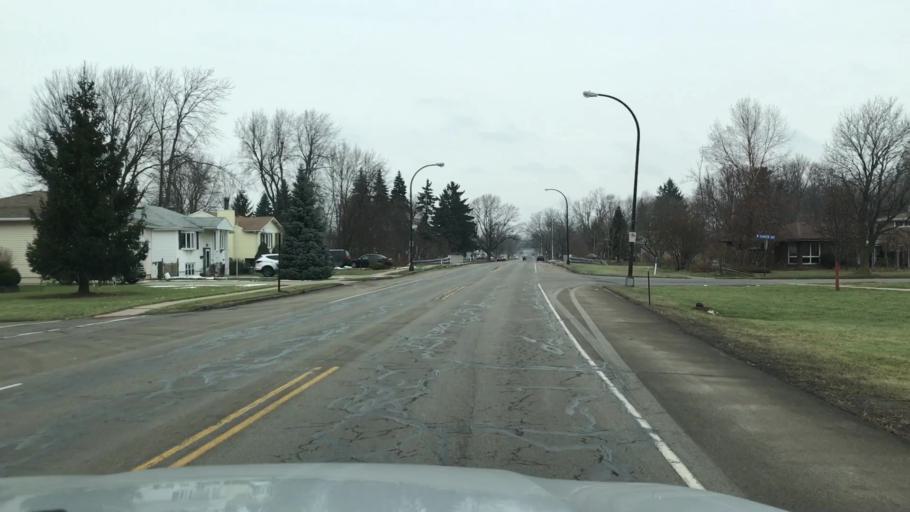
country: US
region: New York
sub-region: Erie County
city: Lackawanna
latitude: 42.8195
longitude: -78.8101
